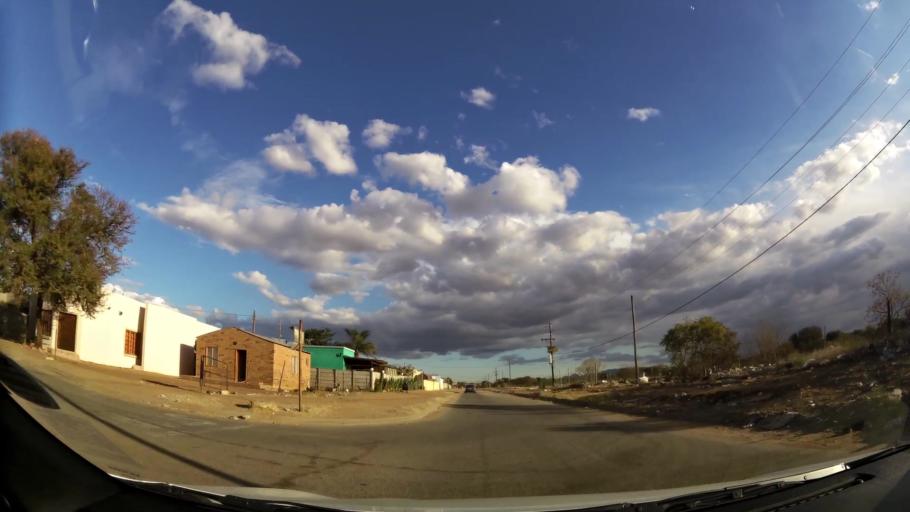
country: ZA
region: Limpopo
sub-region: Capricorn District Municipality
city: Polokwane
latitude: -23.9116
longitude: 29.4238
